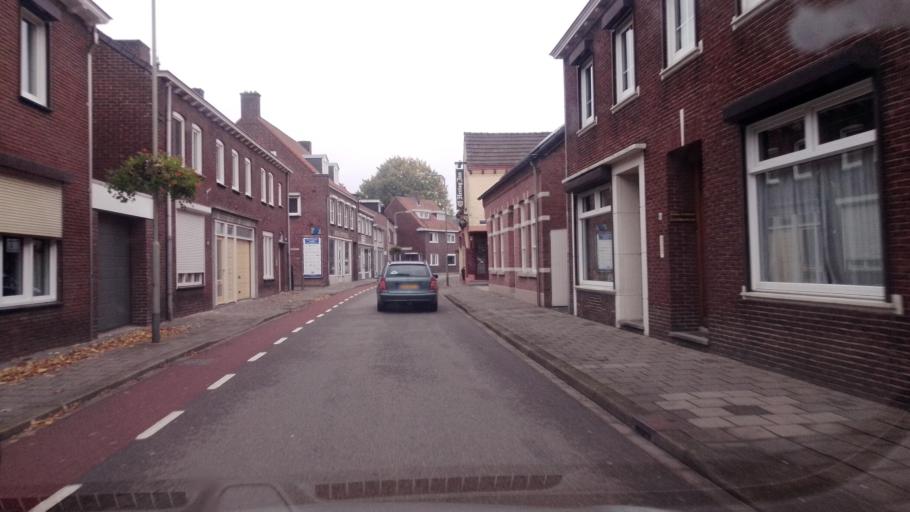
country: NL
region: Limburg
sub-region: Gemeente Peel en Maas
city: Maasbree
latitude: 51.4529
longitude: 6.0543
